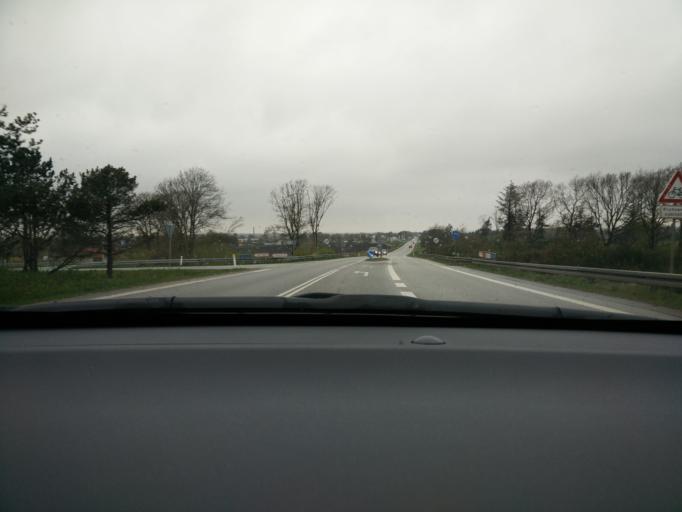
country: DK
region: Central Jutland
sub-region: Skive Kommune
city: Hojslev
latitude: 56.5415
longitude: 9.1356
